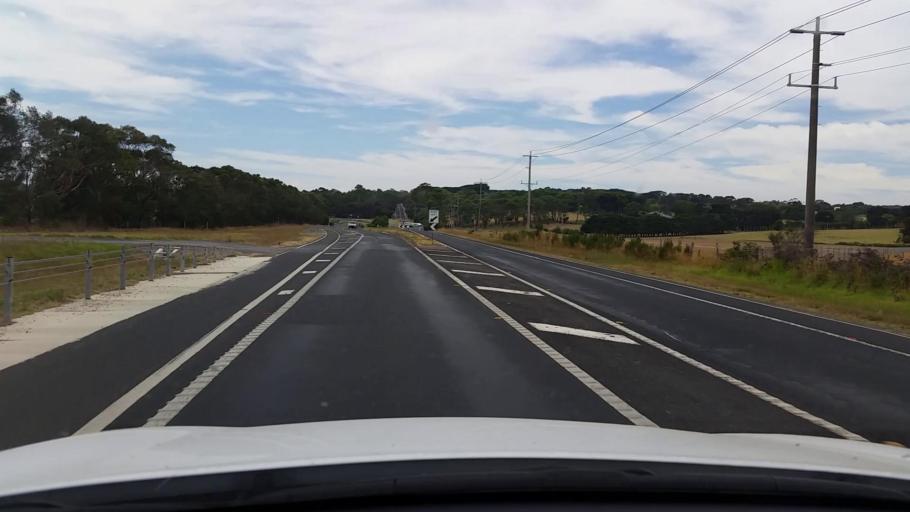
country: AU
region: Victoria
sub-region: Mornington Peninsula
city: Safety Beach
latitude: -38.3124
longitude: 145.0249
